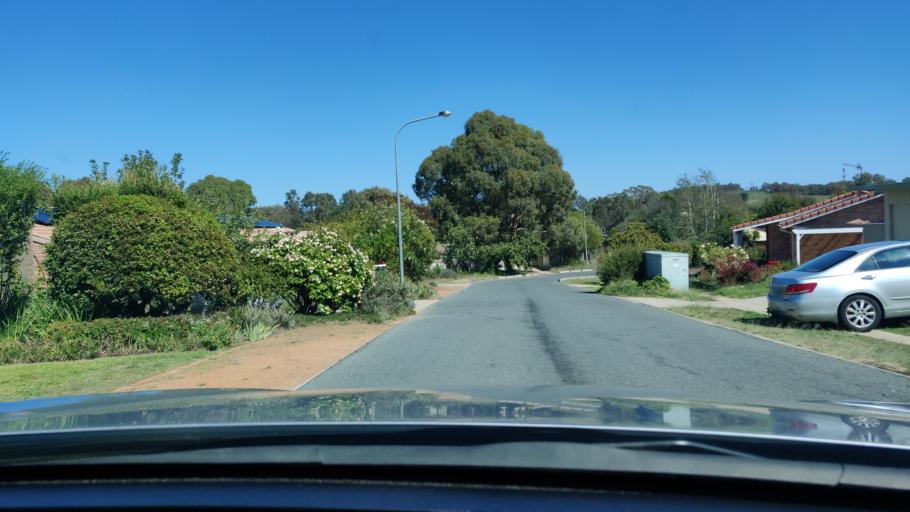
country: AU
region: Australian Capital Territory
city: Macarthur
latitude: -35.4389
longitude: 149.0948
